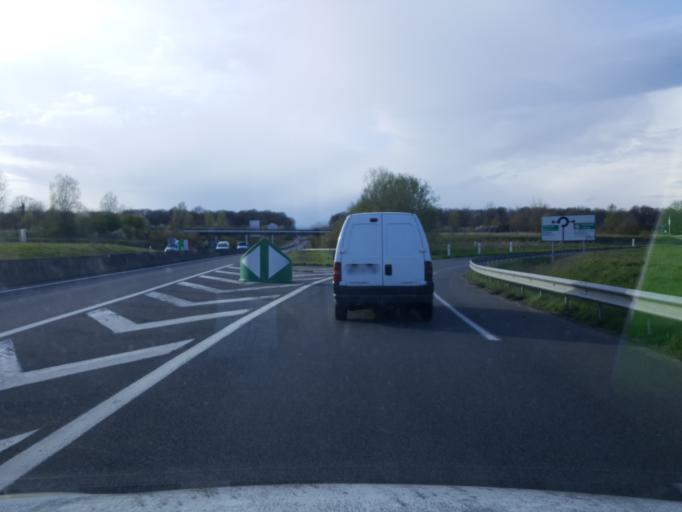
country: FR
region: Picardie
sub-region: Departement de l'Oise
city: Auneuil
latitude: 49.3865
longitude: 2.0139
